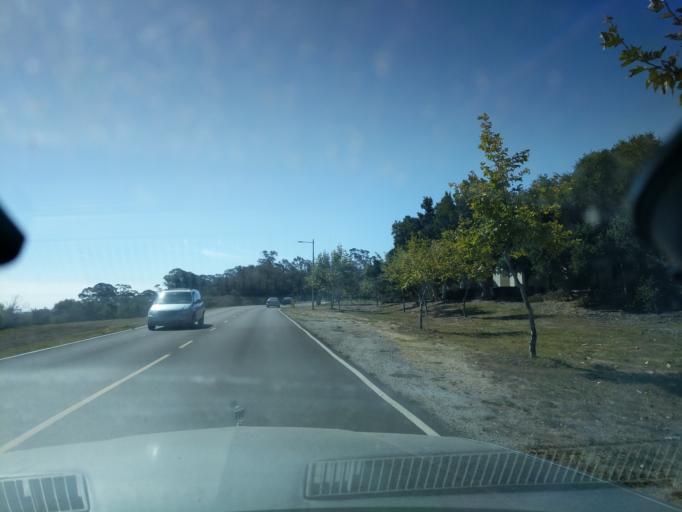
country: US
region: California
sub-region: Santa Barbara County
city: Isla Vista
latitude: 34.4208
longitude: -119.8505
